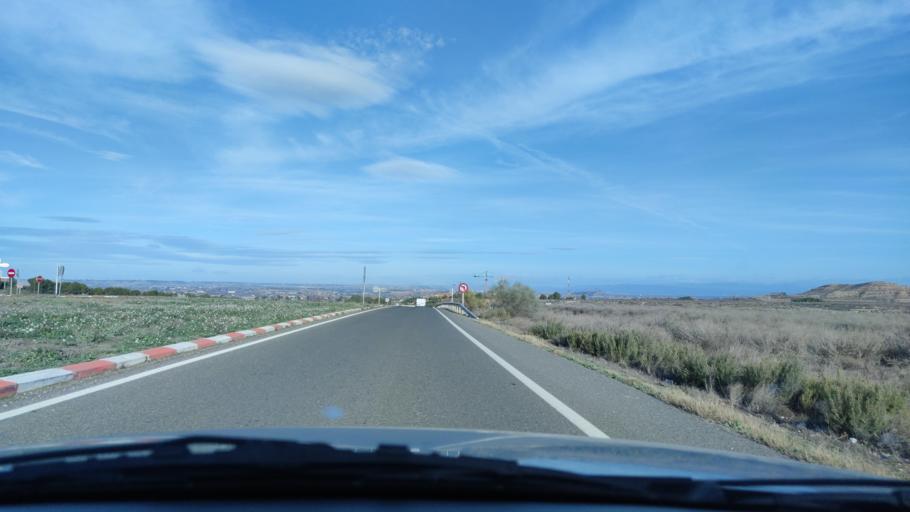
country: ES
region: Catalonia
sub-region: Provincia de Lleida
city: Alfes
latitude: 41.5513
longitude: 0.6245
